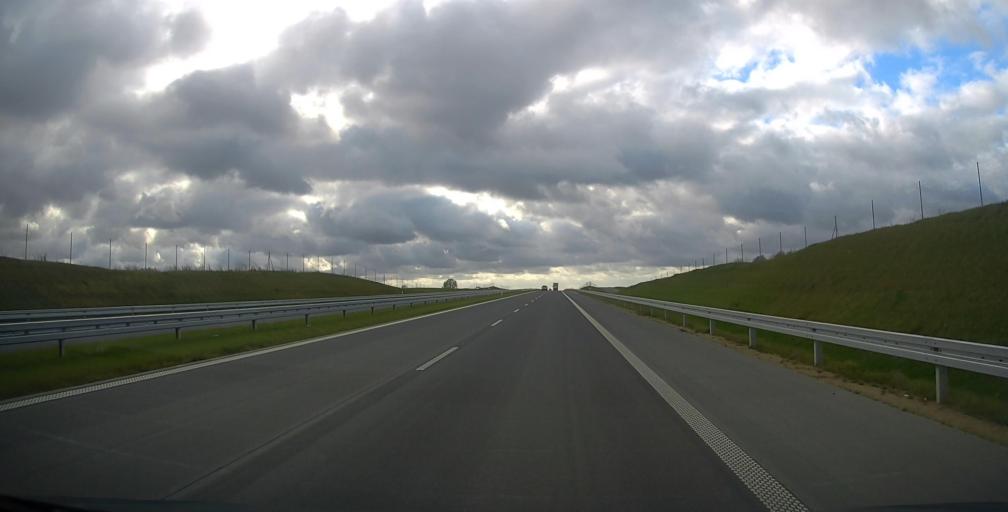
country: PL
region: Podlasie
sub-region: Powiat suwalski
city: Raczki
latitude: 53.8920
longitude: 22.6802
